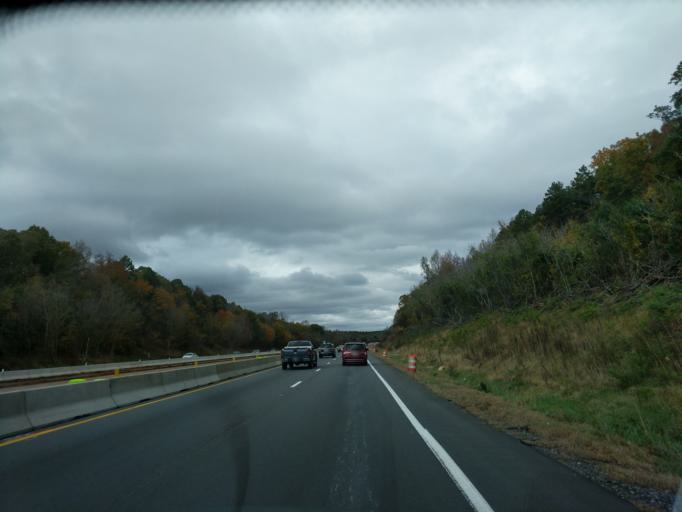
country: US
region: North Carolina
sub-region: Rowan County
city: Landis
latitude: 35.5166
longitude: -80.5691
